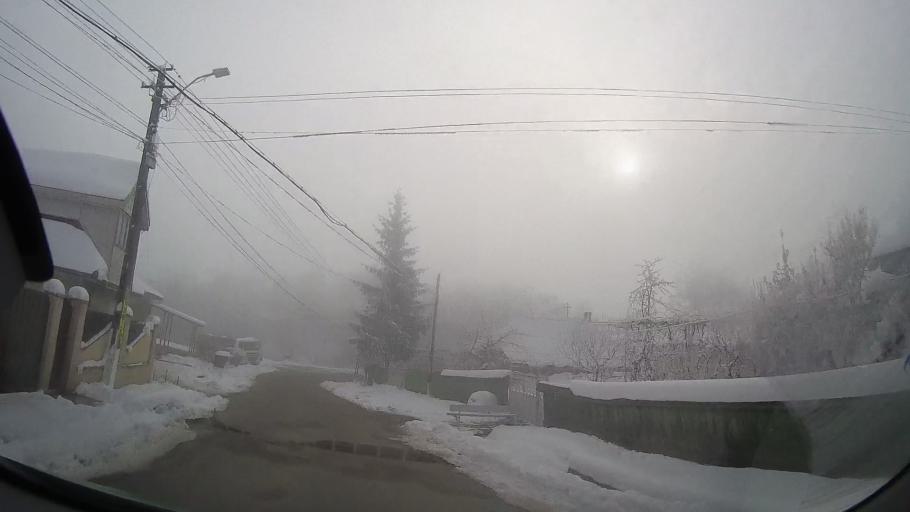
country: RO
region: Iasi
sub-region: Comuna Valea Seaca
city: Topile
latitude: 47.2614
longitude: 26.6675
